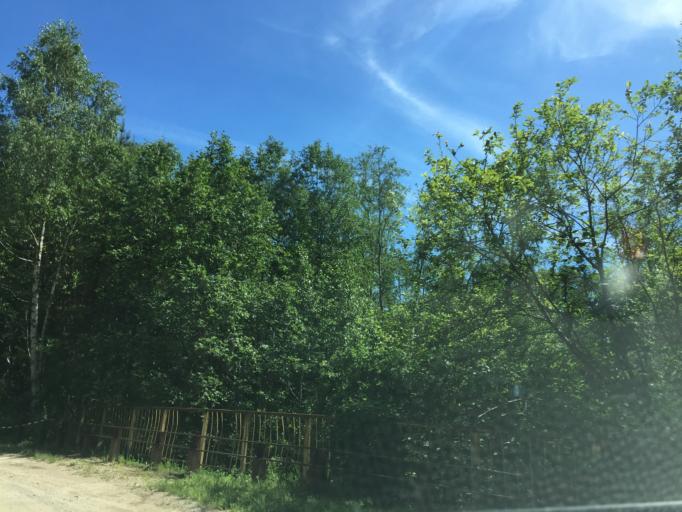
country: LV
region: Kuldigas Rajons
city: Kuldiga
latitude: 57.1158
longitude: 21.8727
